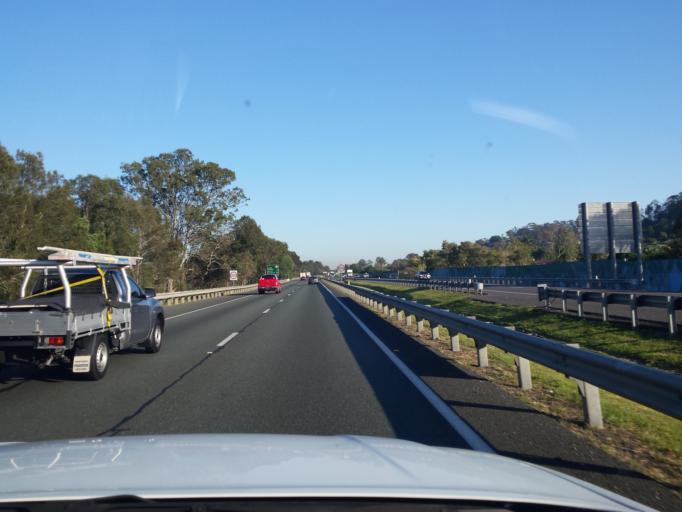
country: AU
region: Queensland
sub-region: Logan
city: Slacks Creek
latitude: -27.6818
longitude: 153.1714
